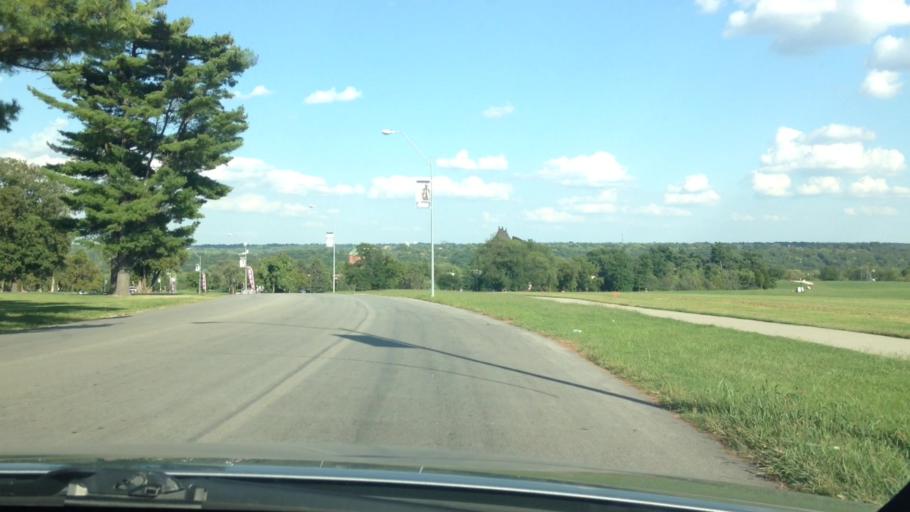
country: US
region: Missouri
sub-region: Jackson County
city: Raytown
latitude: 39.0074
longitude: -94.5386
